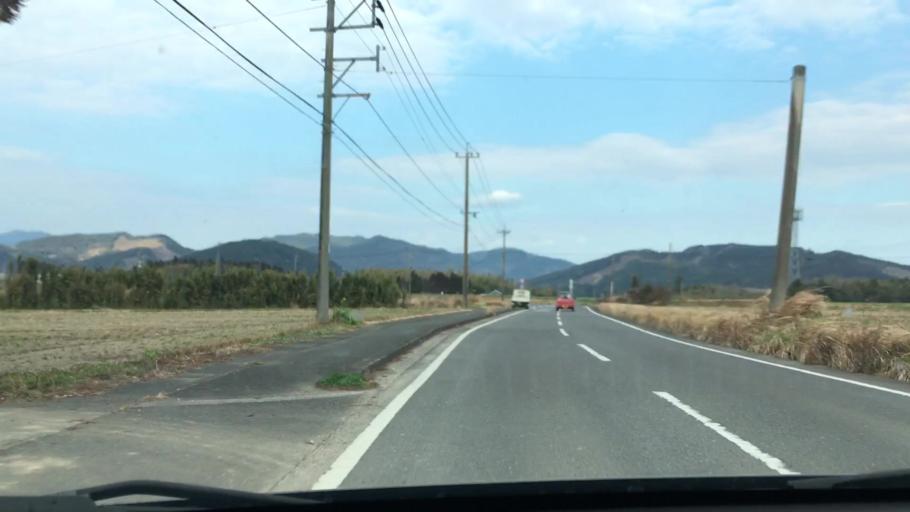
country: JP
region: Miyazaki
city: Kushima
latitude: 31.5058
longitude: 131.2422
